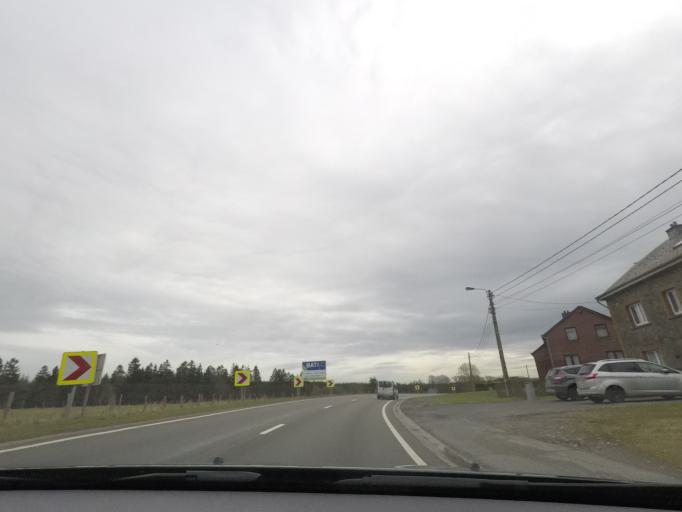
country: BE
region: Wallonia
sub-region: Province du Luxembourg
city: Bastogne
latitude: 49.9897
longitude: 5.7545
